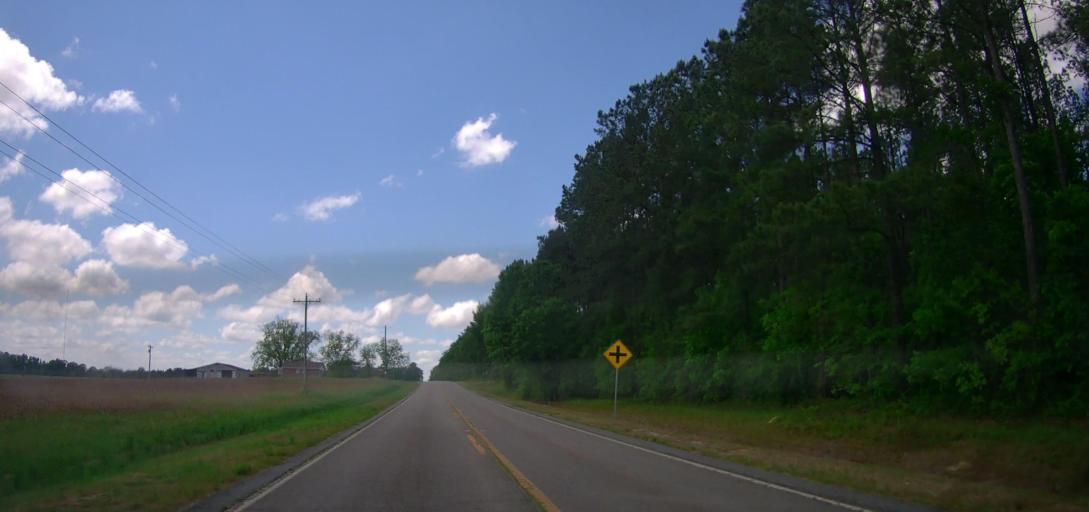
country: US
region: Georgia
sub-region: Dodge County
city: Chester
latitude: 32.4929
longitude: -83.2491
